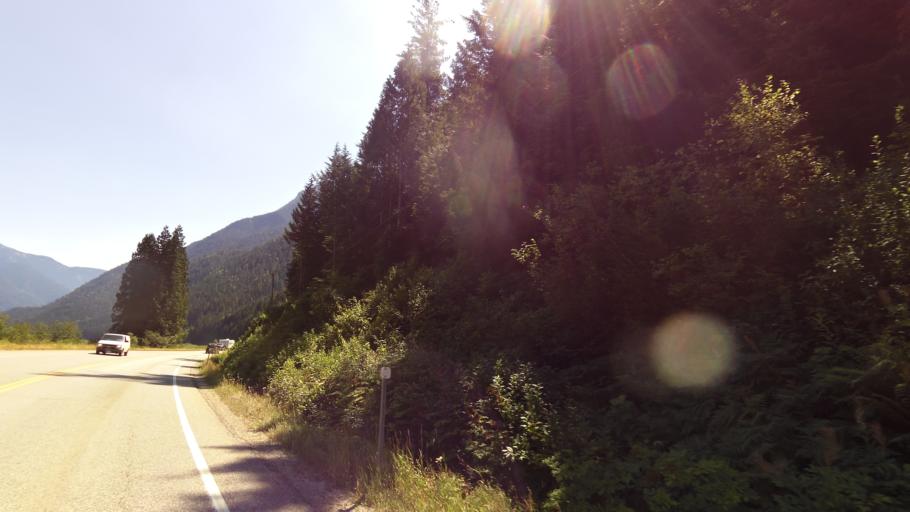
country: CA
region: British Columbia
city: Revelstoke
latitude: 50.9733
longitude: -118.5987
